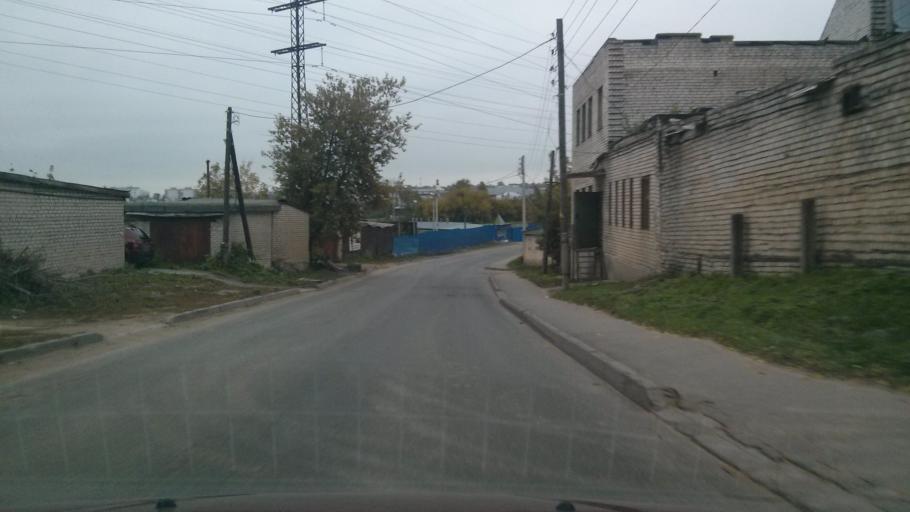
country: RU
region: Nizjnij Novgorod
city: Nizhniy Novgorod
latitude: 56.3084
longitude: 44.0095
